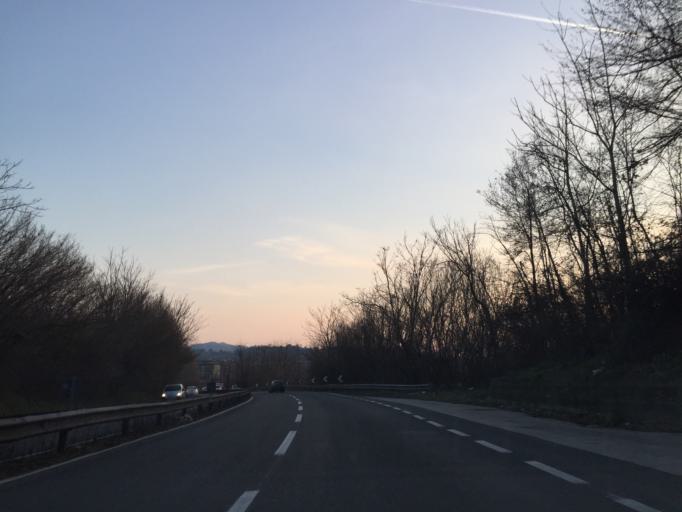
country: IT
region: Campania
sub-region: Provincia di Avellino
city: Atripalda
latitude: 40.9238
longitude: 14.8263
